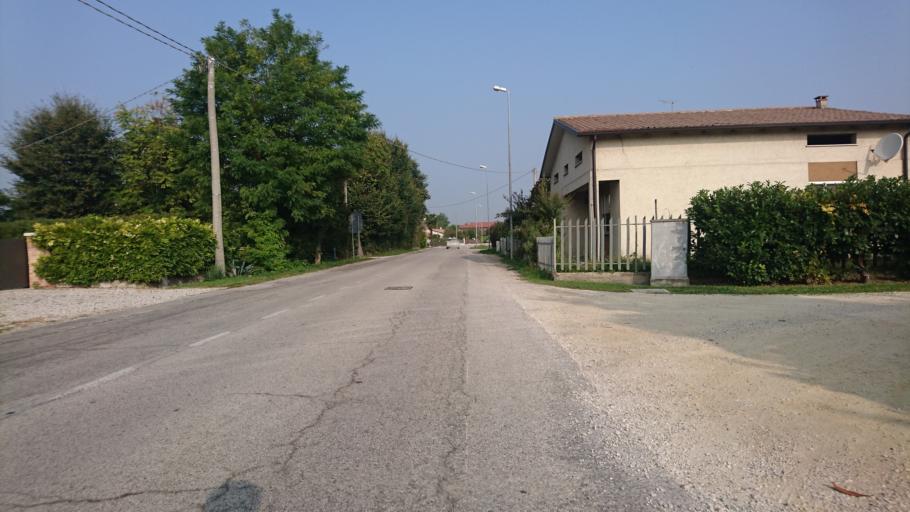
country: IT
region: Veneto
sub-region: Provincia di Padova
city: Pieve
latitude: 45.5390
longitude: 11.8339
